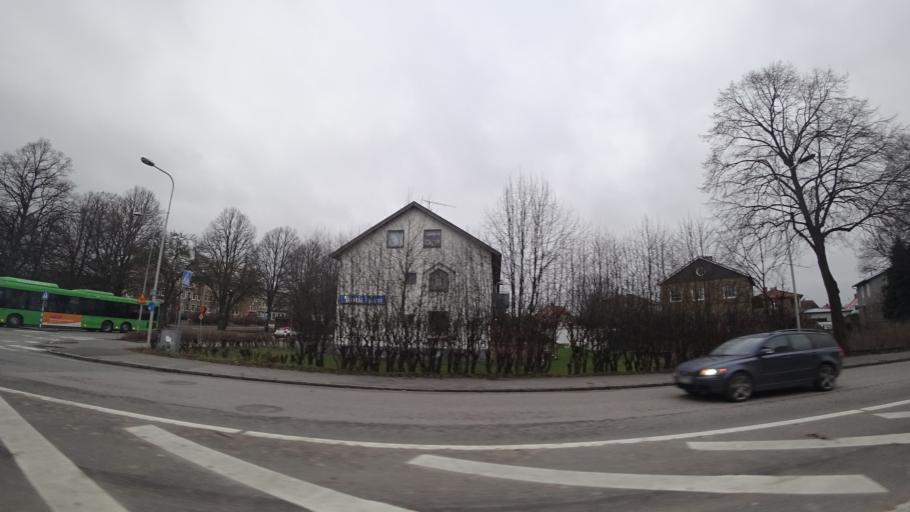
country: SE
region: Skane
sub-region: Kristianstads Kommun
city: Kristianstad
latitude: 56.0384
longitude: 14.1629
